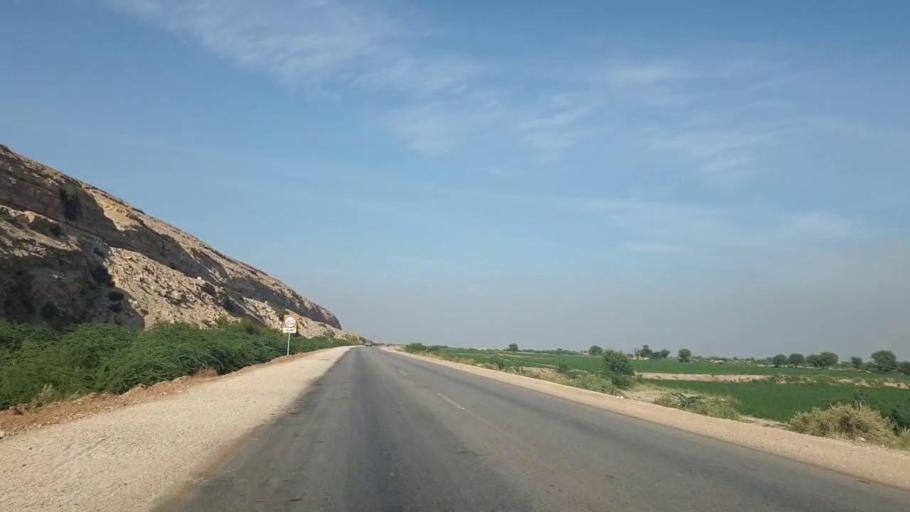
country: PK
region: Sindh
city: Sehwan
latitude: 26.3566
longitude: 67.8731
